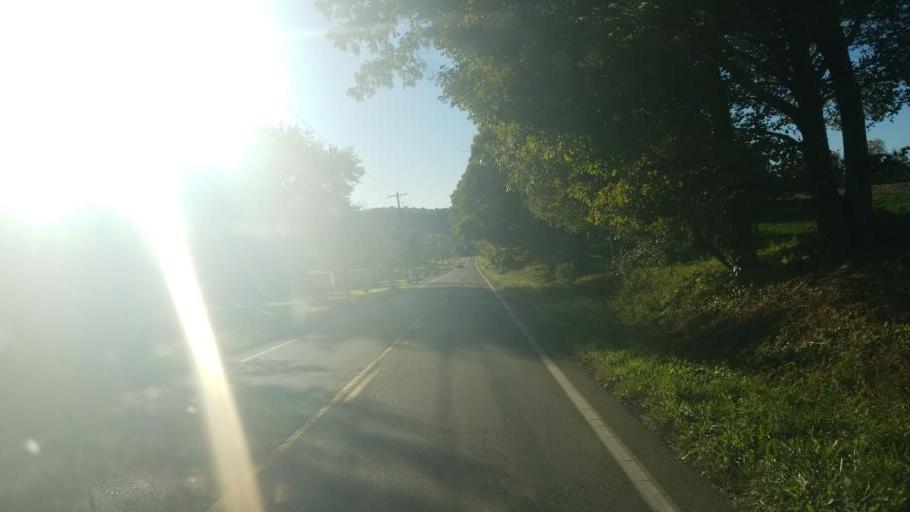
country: US
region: Ohio
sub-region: Columbiana County
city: Leetonia
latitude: 40.9008
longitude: -80.7788
